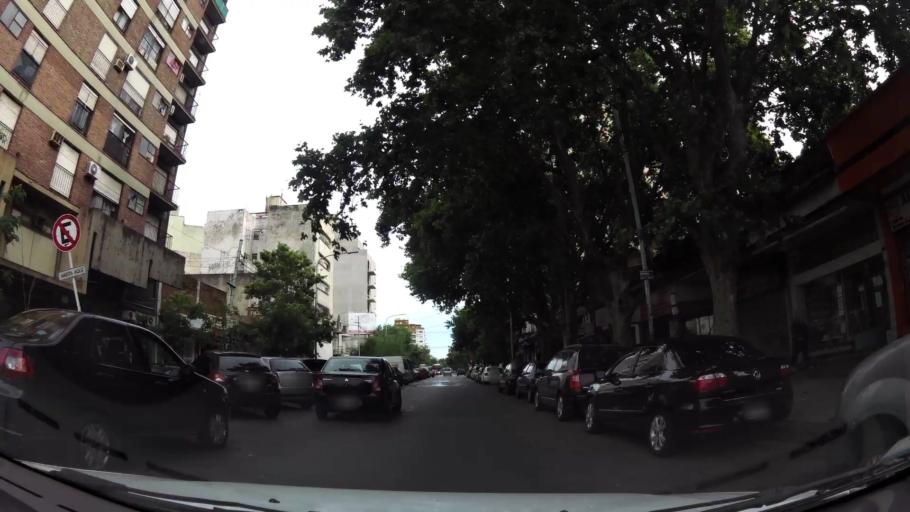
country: AR
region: Buenos Aires F.D.
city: Villa Santa Rita
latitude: -34.6356
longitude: -58.4876
